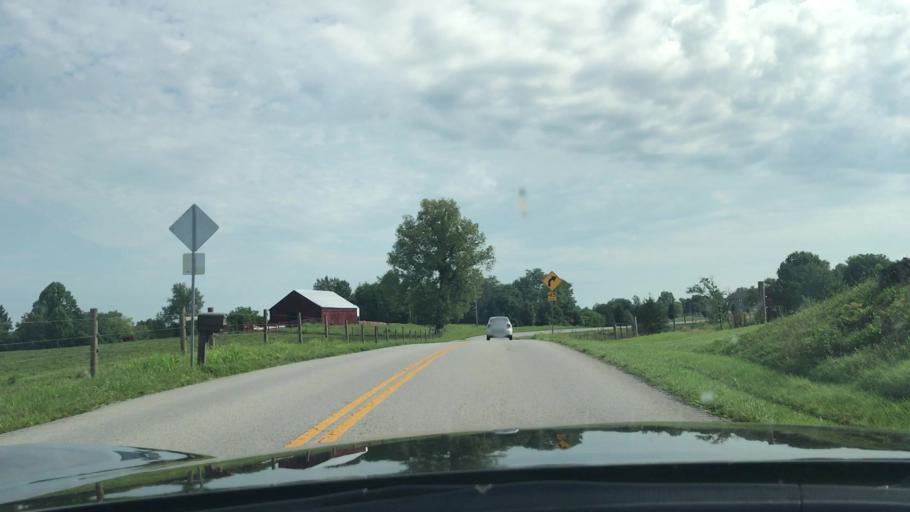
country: US
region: Kentucky
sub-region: Green County
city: Greensburg
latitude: 37.2655
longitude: -85.5449
